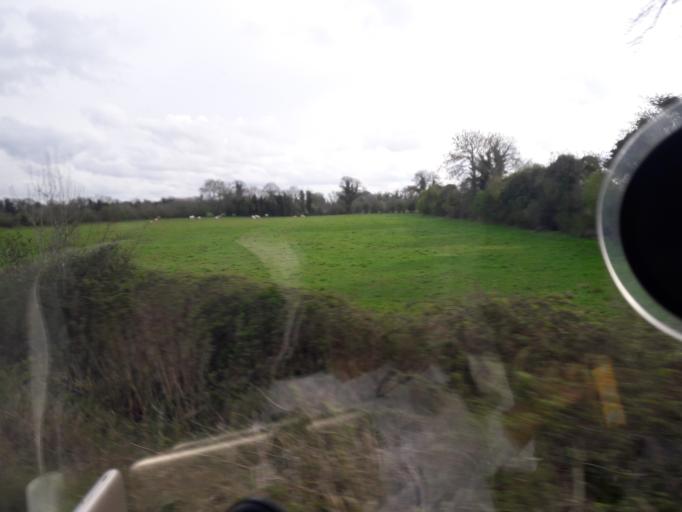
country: IE
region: Leinster
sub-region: An Mhi
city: Longwood
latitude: 53.4393
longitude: -6.9250
